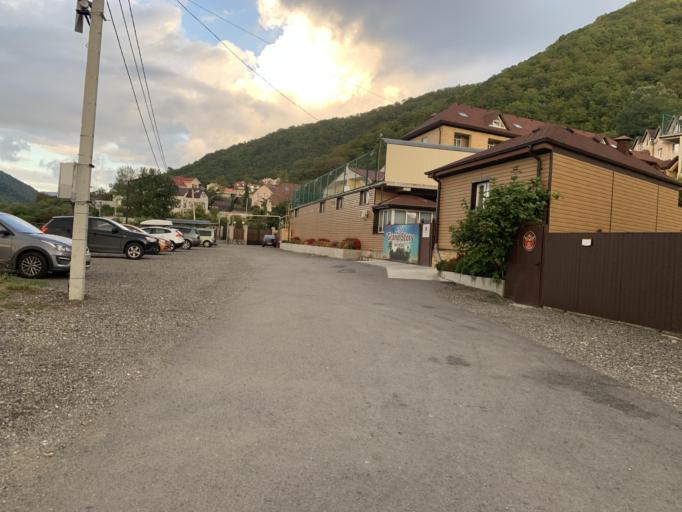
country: RU
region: Krasnodarskiy
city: Nebug
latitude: 44.1657
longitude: 39.0024
